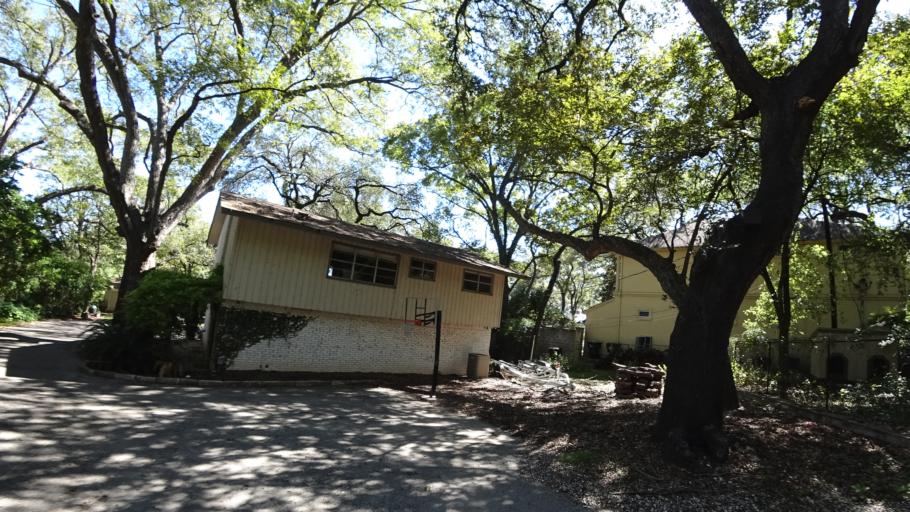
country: US
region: Texas
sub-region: Travis County
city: West Lake Hills
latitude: 30.3124
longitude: -97.7799
